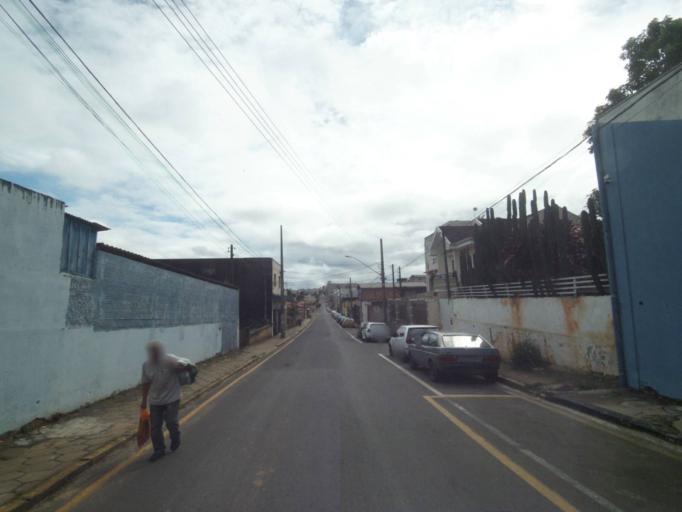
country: BR
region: Parana
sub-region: Telemaco Borba
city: Telemaco Borba
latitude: -24.3263
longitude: -50.6249
